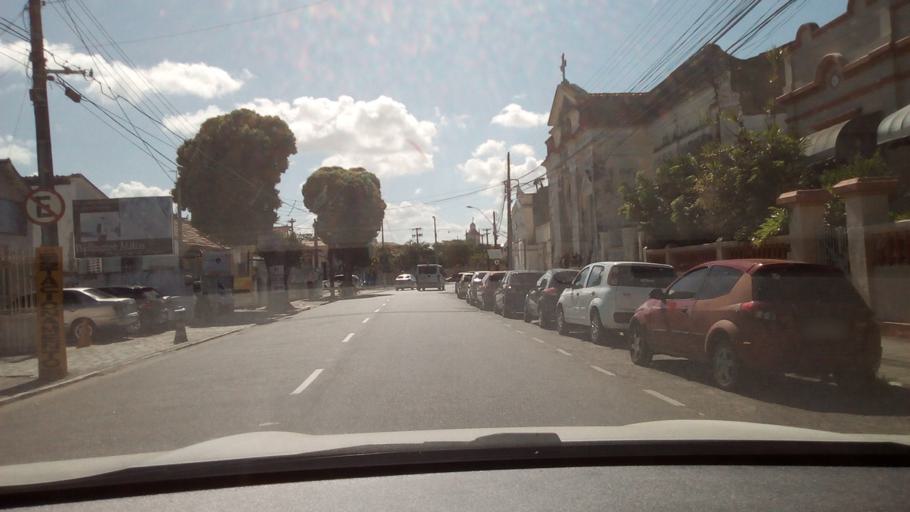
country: BR
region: Paraiba
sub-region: Joao Pessoa
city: Joao Pessoa
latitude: -7.1155
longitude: -34.8810
